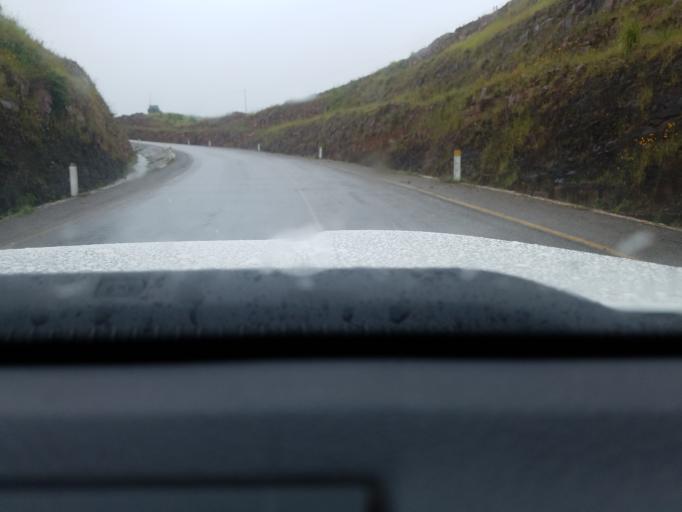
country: TZ
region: Kigoma
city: Mwandiga
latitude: -4.6667
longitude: 29.7258
